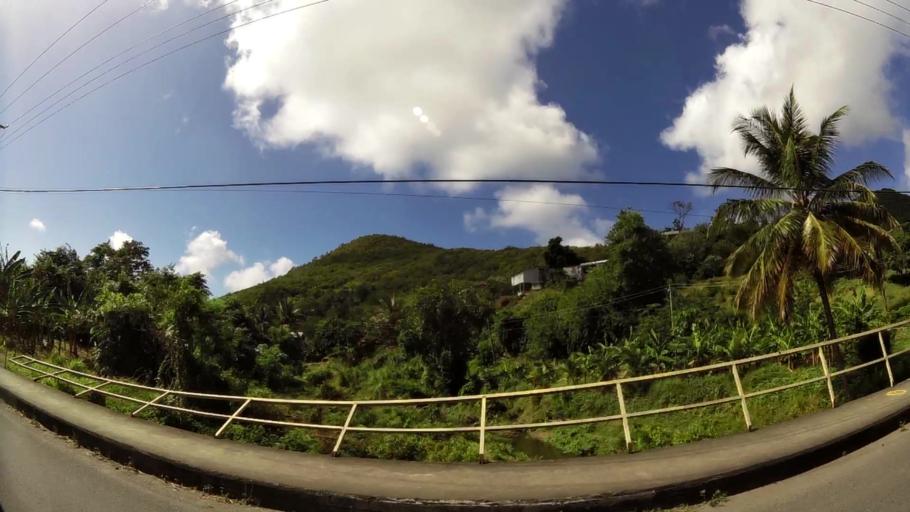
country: LC
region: Laborie Quarter
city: Laborie
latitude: 13.7459
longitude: -60.9851
